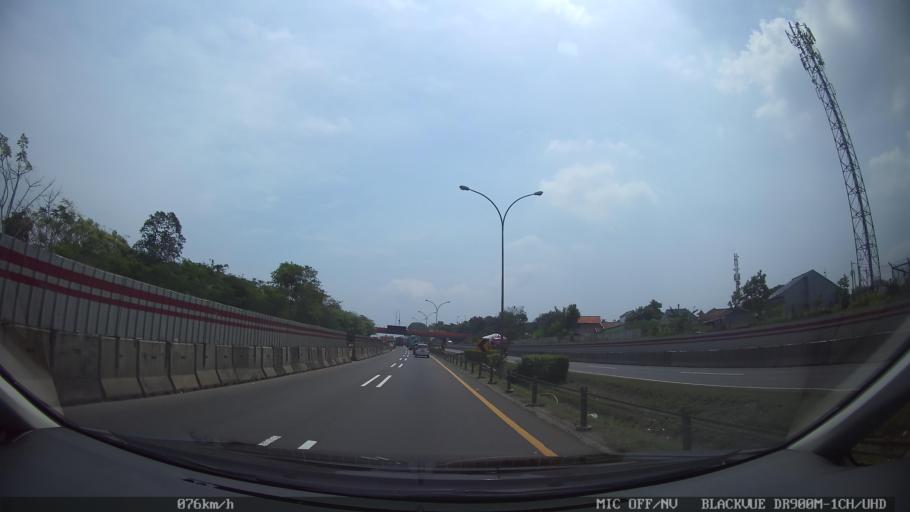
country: ID
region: West Java
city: Kresek
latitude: -6.1434
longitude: 106.2884
